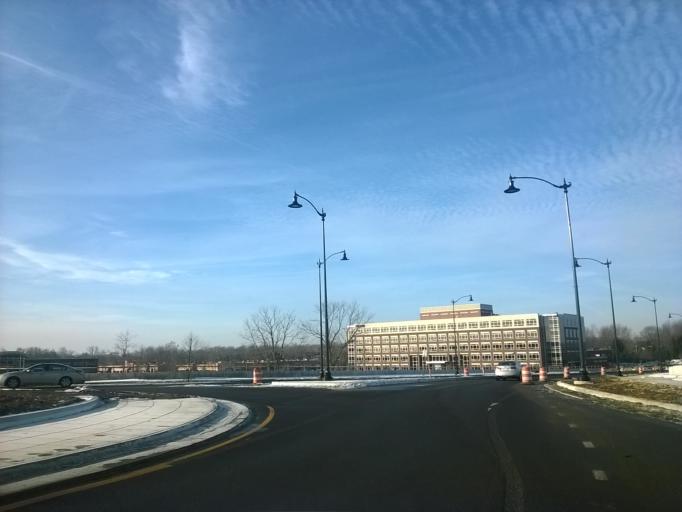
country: US
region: Indiana
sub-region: Hamilton County
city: Carmel
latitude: 39.9781
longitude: -86.1581
